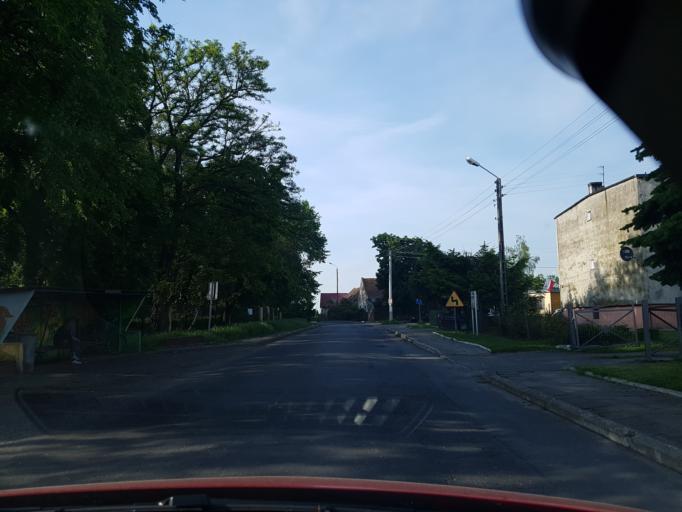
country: PL
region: Lower Silesian Voivodeship
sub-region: Powiat strzelinski
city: Wiazow
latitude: 50.8542
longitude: 17.1856
